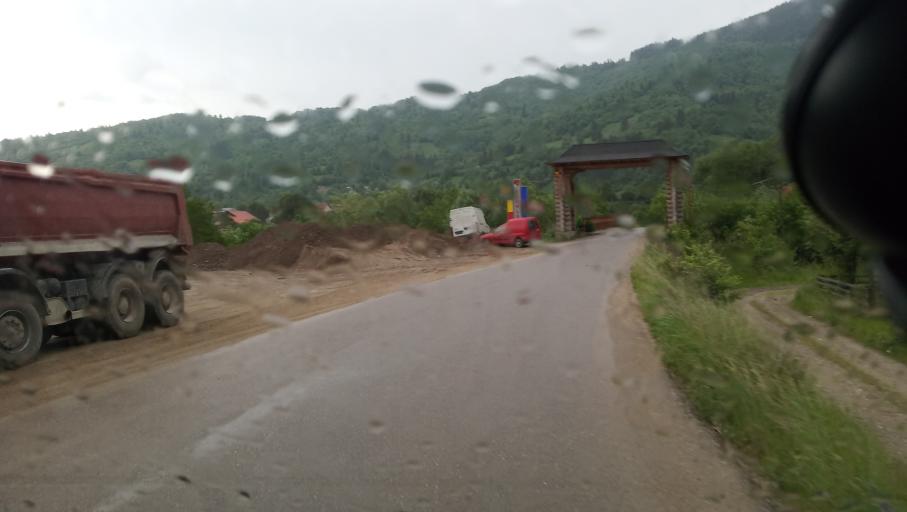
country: RO
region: Neamt
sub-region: Comuna Ceahlau
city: Ceahlau
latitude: 47.0570
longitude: 25.9209
